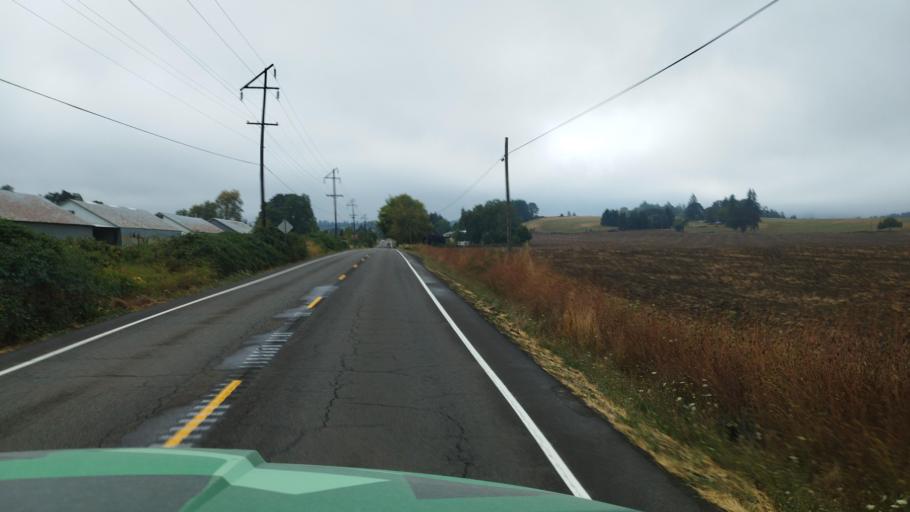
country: US
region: Oregon
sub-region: Washington County
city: Forest Grove
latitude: 45.4279
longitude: -123.1379
